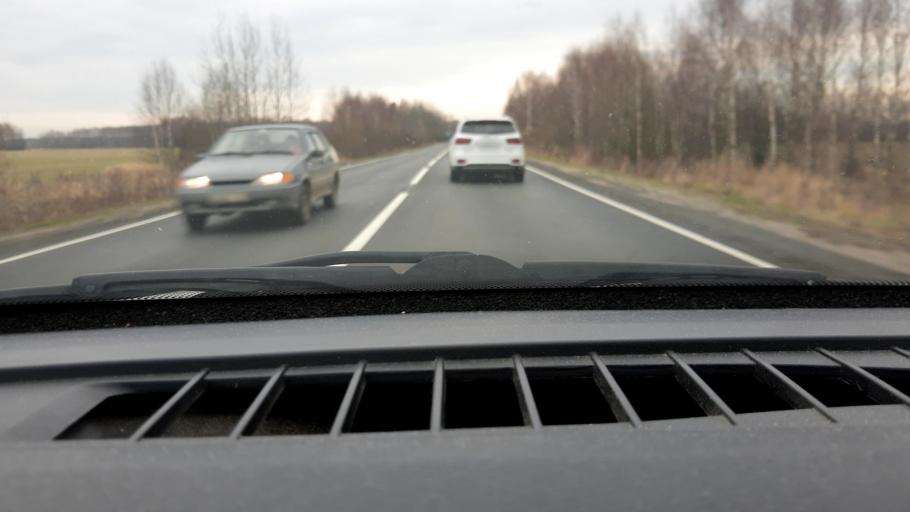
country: RU
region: Nizjnij Novgorod
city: Novaya Balakhna
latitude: 56.5756
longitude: 43.6992
